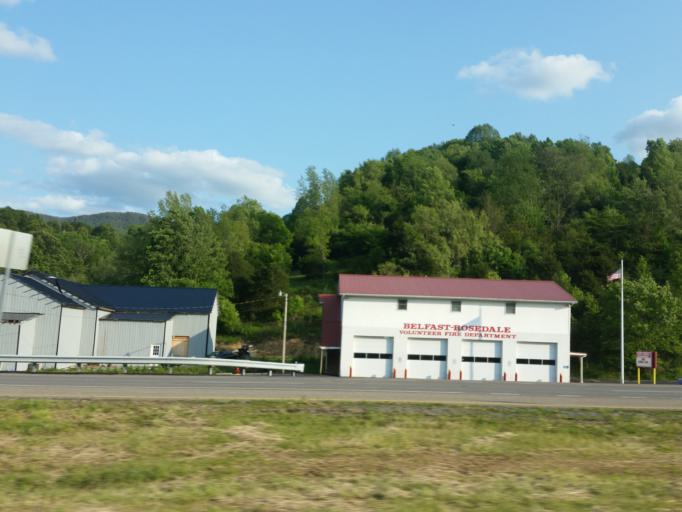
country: US
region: Virginia
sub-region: Tazewell County
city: Raven
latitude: 36.9795
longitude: -81.8681
